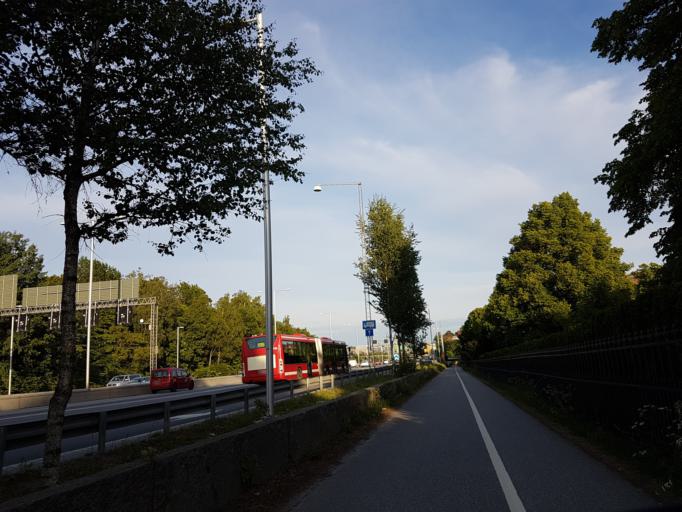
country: SE
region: Stockholm
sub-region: Norrtalje Kommun
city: Bergshamra
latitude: 59.3568
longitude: 18.0318
